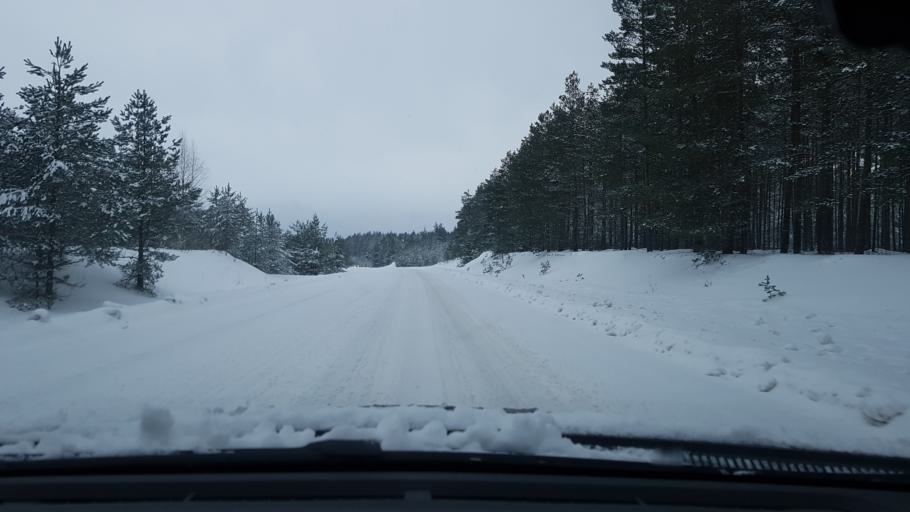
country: EE
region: Harju
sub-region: Kuusalu vald
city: Kuusalu
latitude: 59.4277
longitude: 25.3859
